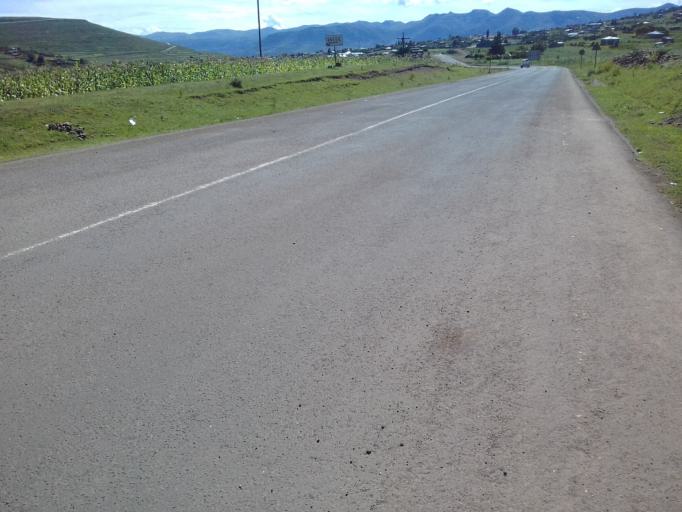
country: LS
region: Thaba-Tseka
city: Thaba-Tseka
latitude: -29.5195
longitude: 28.5824
